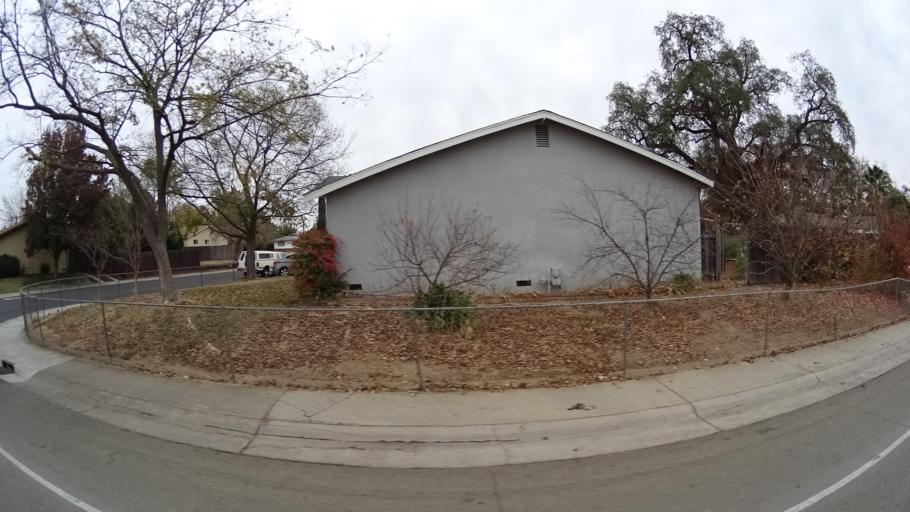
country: US
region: California
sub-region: Sacramento County
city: Citrus Heights
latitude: 38.6972
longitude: -121.2948
